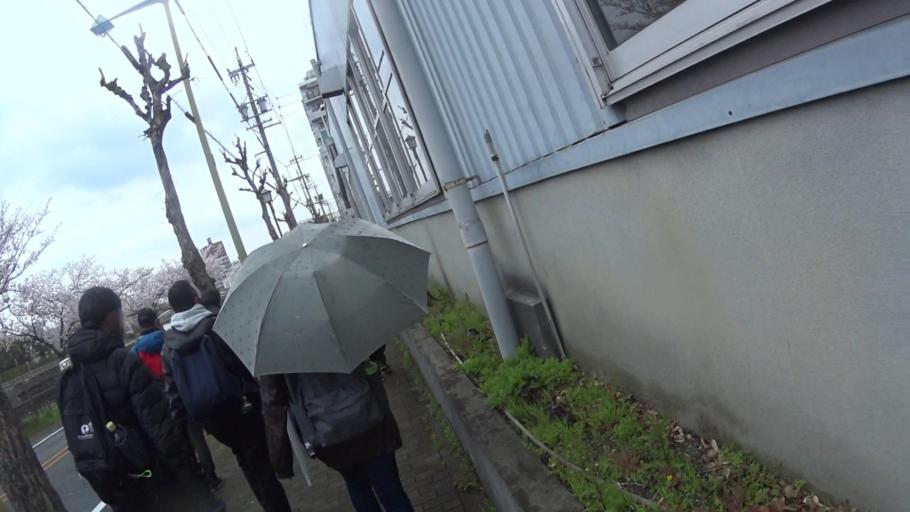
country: JP
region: Aichi
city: Nagoya-shi
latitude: 35.1249
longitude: 136.9025
